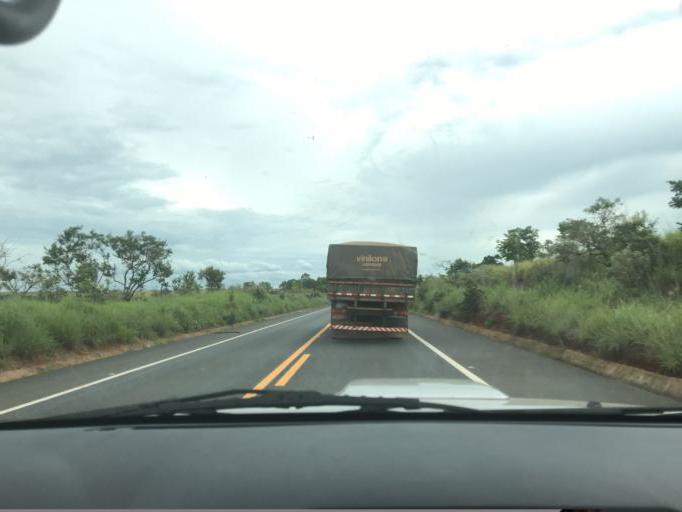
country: BR
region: Minas Gerais
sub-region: Araxa
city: Araxa
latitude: -19.3707
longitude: -46.8559
